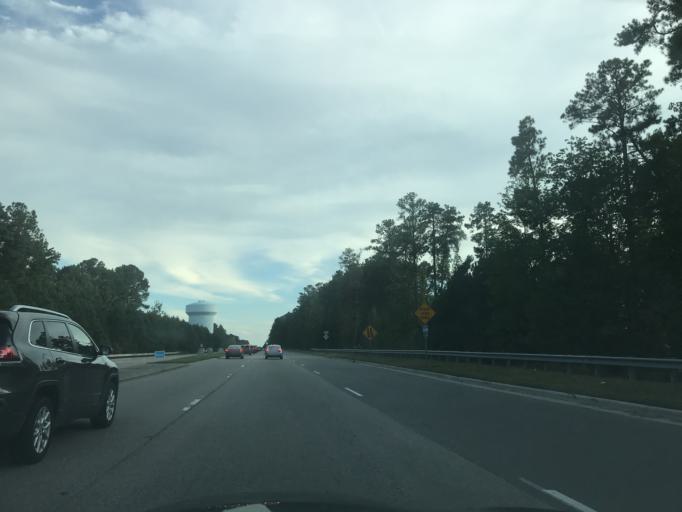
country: US
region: North Carolina
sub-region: Wake County
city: Morrisville
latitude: 35.8201
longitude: -78.8738
